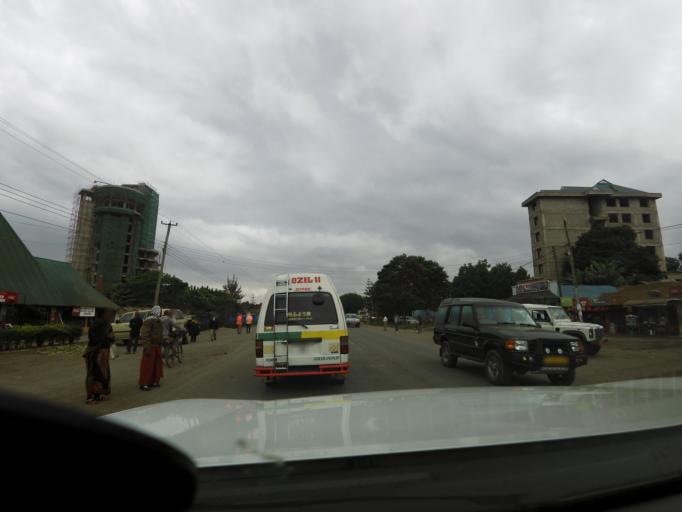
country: TZ
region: Arusha
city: Arusha
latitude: -3.3630
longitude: 36.6739
